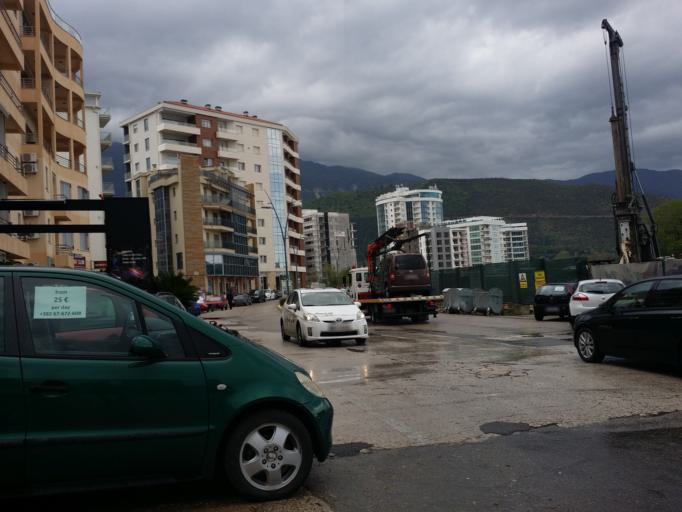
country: ME
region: Budva
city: Budva
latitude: 42.2845
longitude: 18.8384
